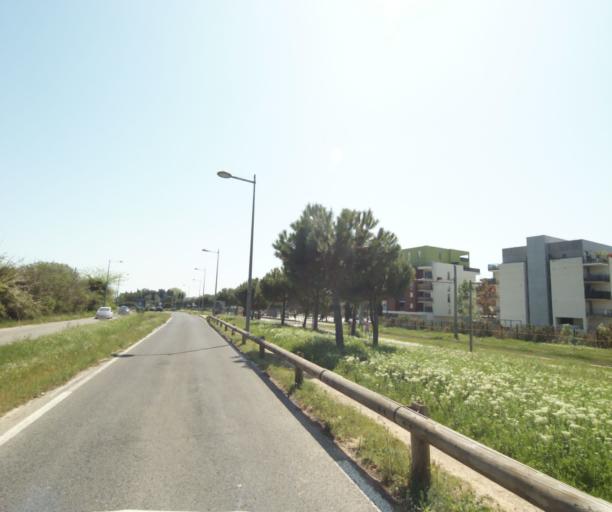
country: FR
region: Languedoc-Roussillon
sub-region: Departement de l'Herault
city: Juvignac
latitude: 43.6354
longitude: 3.8326
